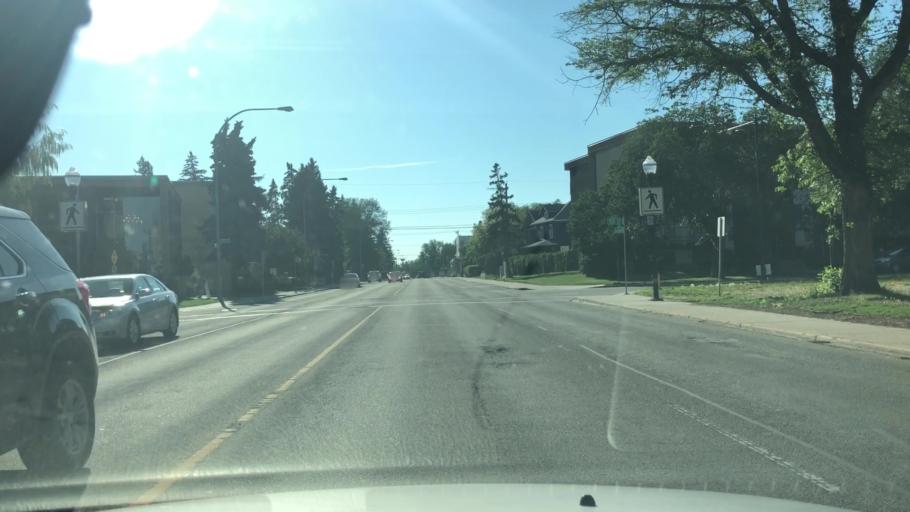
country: CA
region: Alberta
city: Edmonton
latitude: 53.5471
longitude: -113.5370
